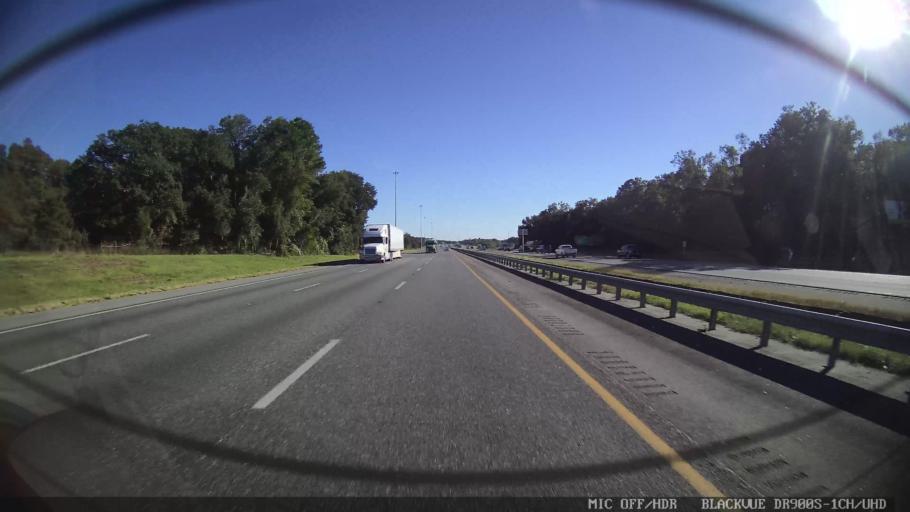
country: US
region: Florida
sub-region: Marion County
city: Ocala
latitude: 29.2745
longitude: -82.1952
